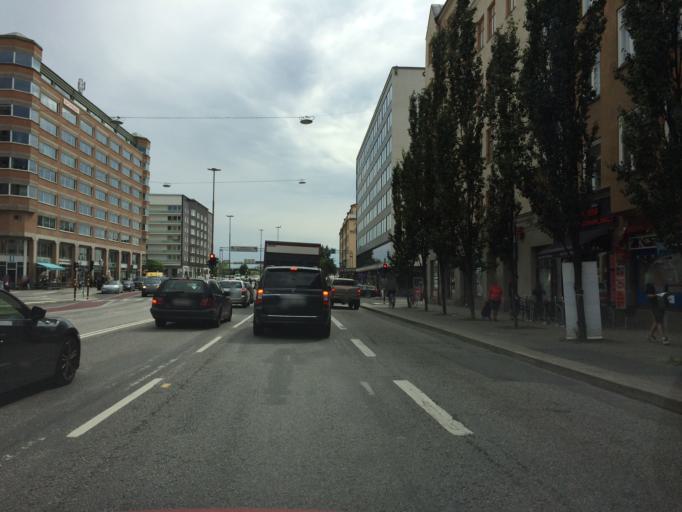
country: SE
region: Stockholm
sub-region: Stockholms Kommun
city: Arsta
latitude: 59.3165
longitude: 18.0333
